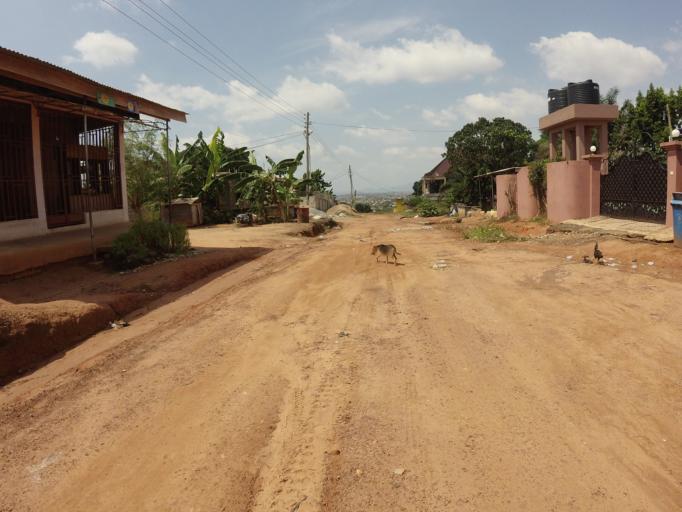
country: GH
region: Greater Accra
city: Gbawe
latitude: 5.6187
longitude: -0.3109
